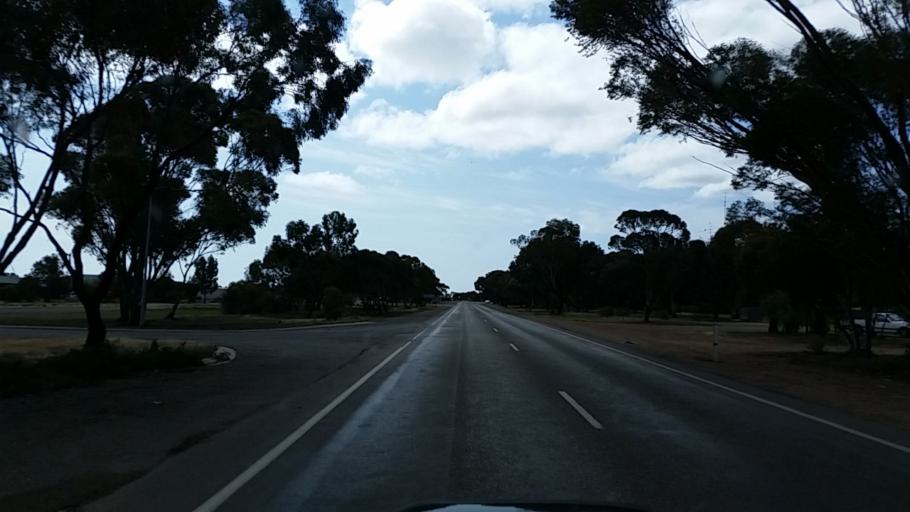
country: AU
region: South Australia
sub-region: Port Pirie City and Dists
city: Port Pirie
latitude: -33.2167
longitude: 138.0110
